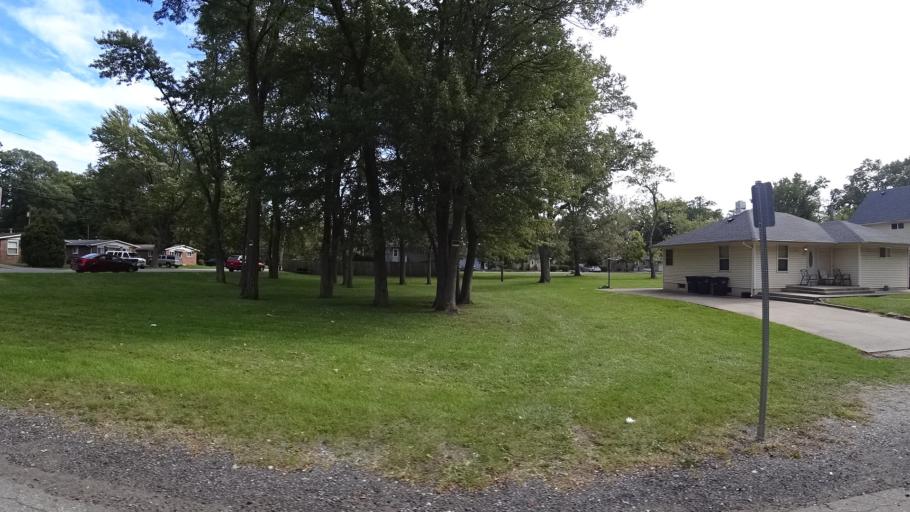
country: US
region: Indiana
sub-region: LaPorte County
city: Michigan City
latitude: 41.7140
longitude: -86.8776
